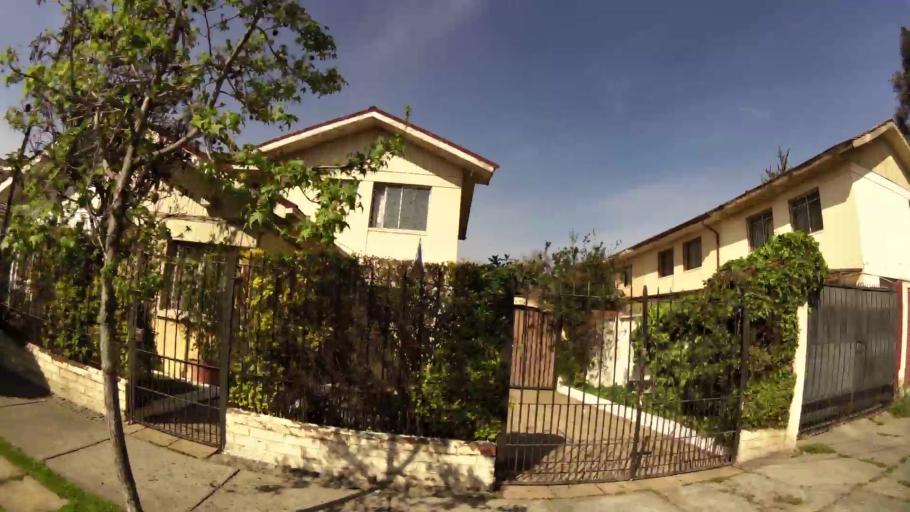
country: CL
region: Santiago Metropolitan
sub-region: Provincia de Santiago
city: La Pintana
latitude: -33.5323
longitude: -70.5922
